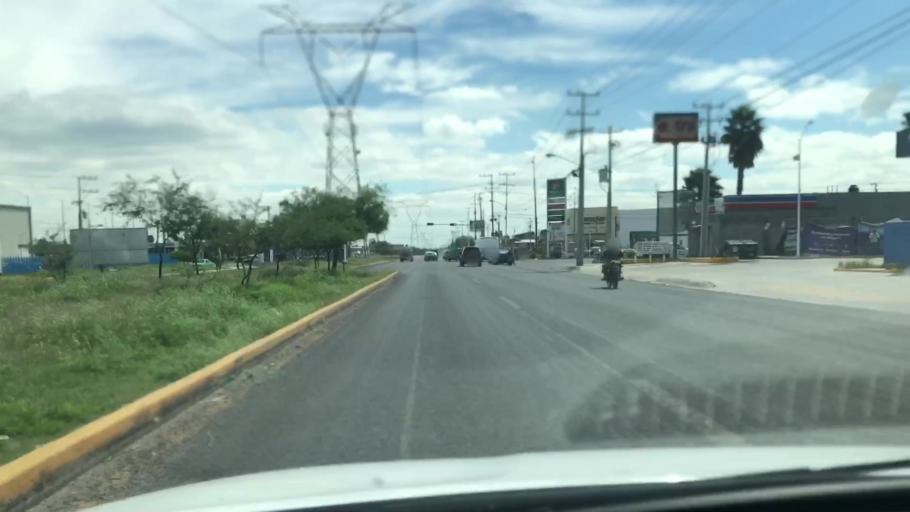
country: MX
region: Guanajuato
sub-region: Celaya
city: La Trinidad
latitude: 20.5497
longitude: -100.7953
